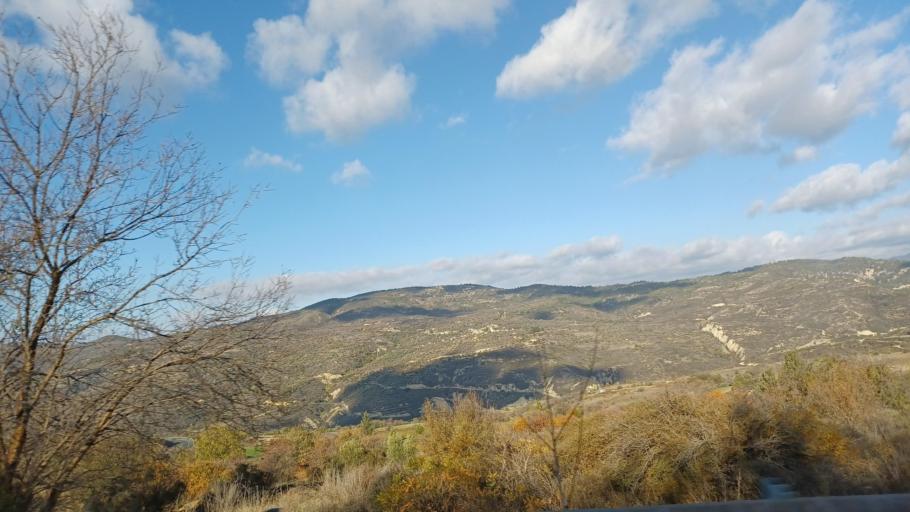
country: CY
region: Limassol
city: Pachna
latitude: 34.8497
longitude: 32.7405
